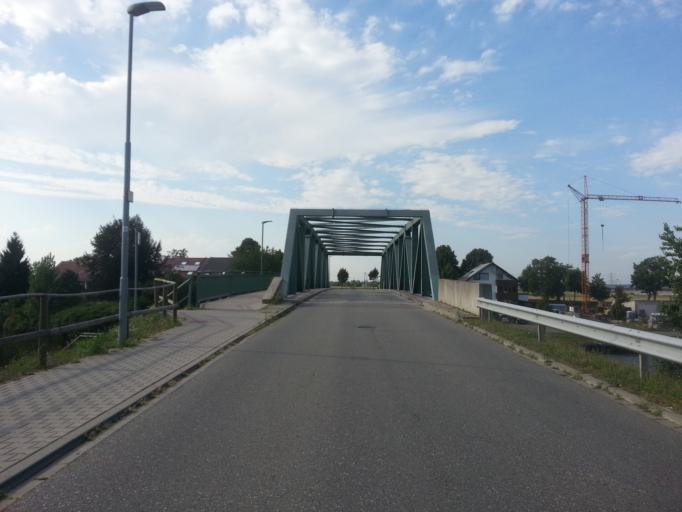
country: DE
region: Baden-Wuerttemberg
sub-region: Karlsruhe Region
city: Ilvesheim
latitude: 49.4800
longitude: 8.5662
